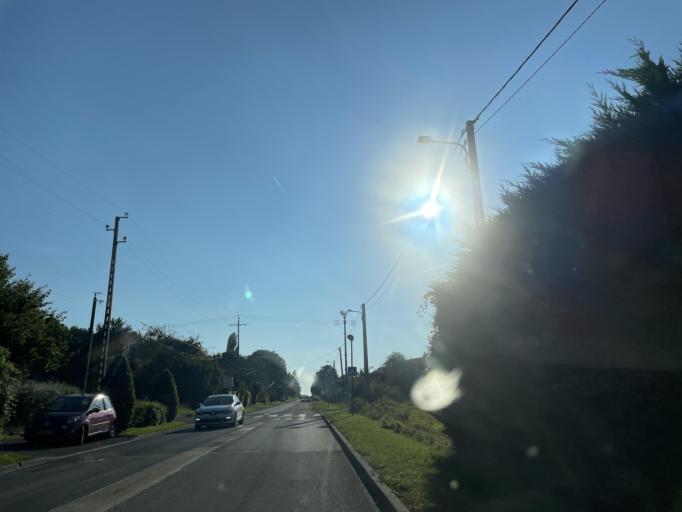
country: FR
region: Ile-de-France
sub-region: Departement de Seine-et-Marne
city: Voulangis
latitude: 48.8495
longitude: 2.8977
